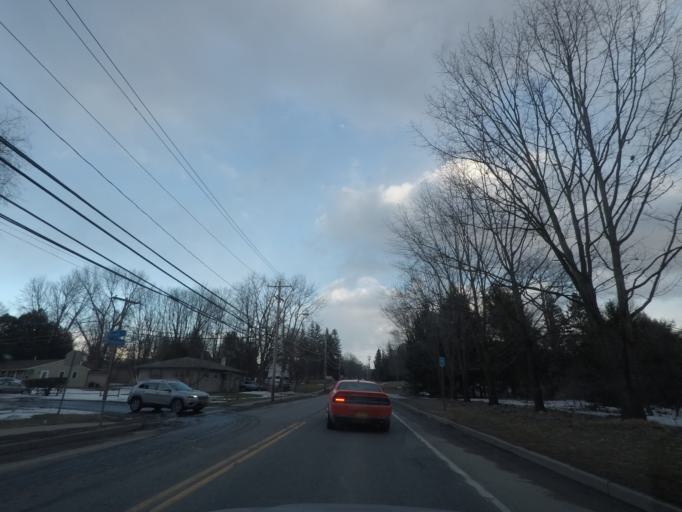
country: US
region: New York
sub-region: Oneida County
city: Utica
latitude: 43.1090
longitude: -75.1751
